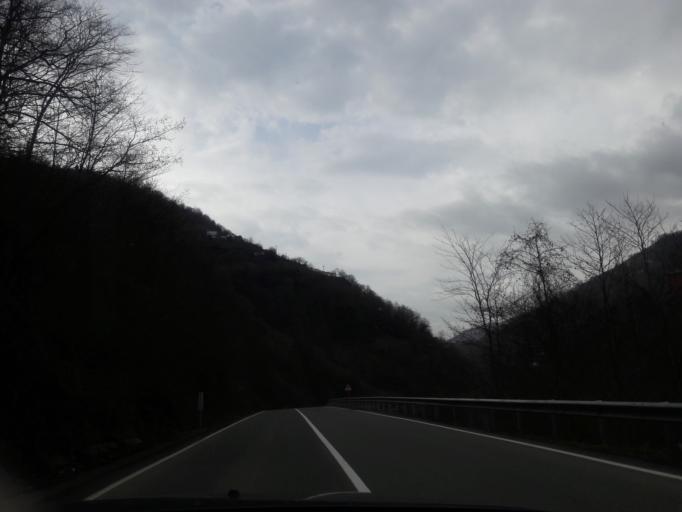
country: TR
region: Trabzon
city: Salpazari
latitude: 40.9720
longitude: 39.1981
